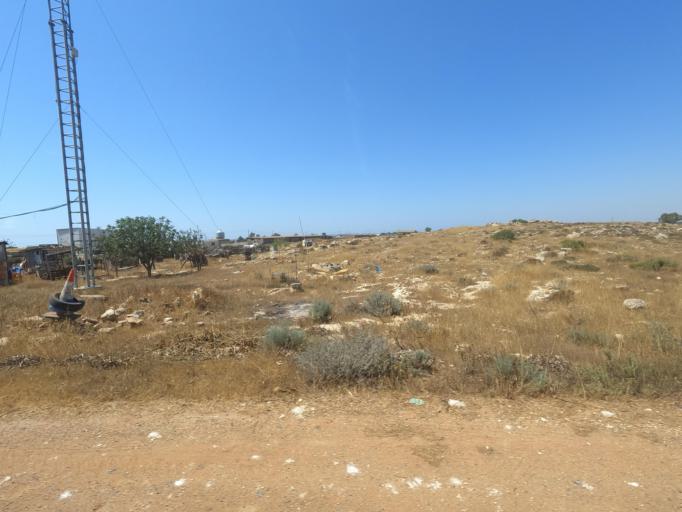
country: CY
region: Ammochostos
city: Liopetri
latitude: 35.0220
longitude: 33.8804
